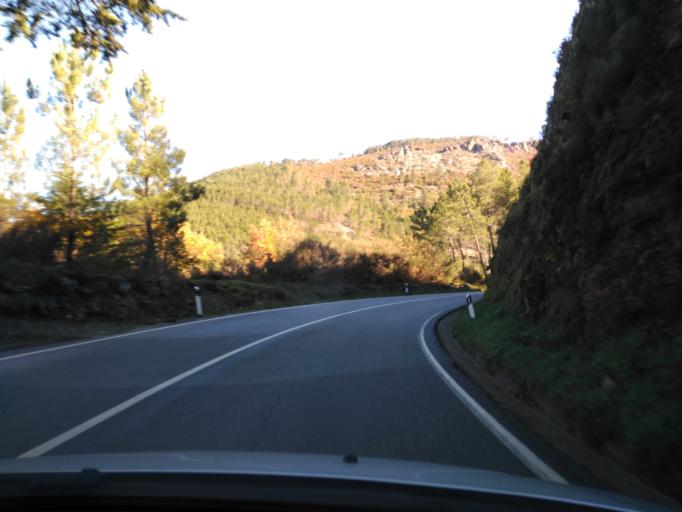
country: PT
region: Braga
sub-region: Cabeceiras de Basto
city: Cabeceiras de Basto
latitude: 41.6682
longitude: -7.9861
